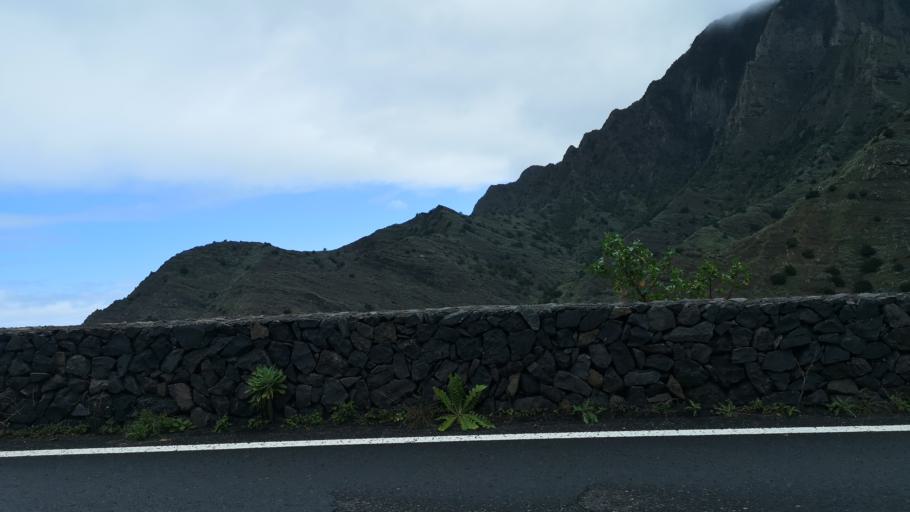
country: ES
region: Canary Islands
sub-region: Provincia de Santa Cruz de Tenerife
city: Hermigua
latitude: 28.1464
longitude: -17.1990
